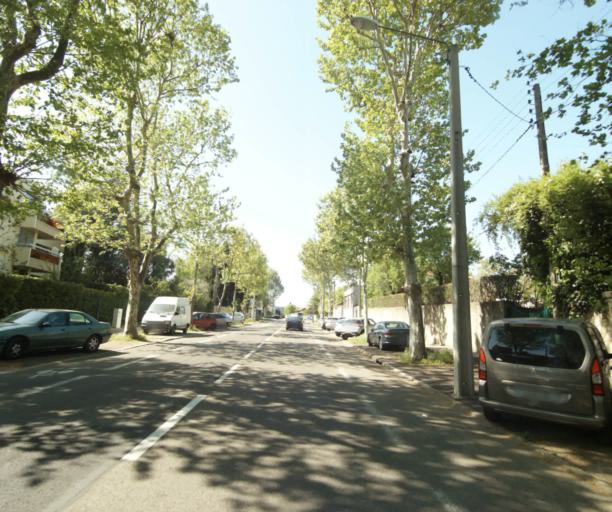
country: FR
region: Languedoc-Roussillon
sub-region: Departement de l'Herault
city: Montpellier
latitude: 43.6161
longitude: 3.8556
